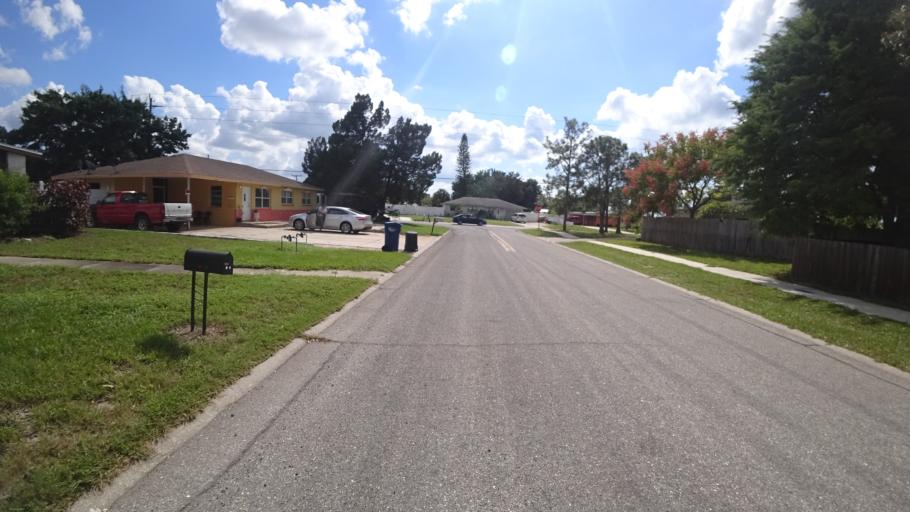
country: US
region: Florida
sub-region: Manatee County
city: Bayshore Gardens
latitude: 27.4232
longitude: -82.5853
